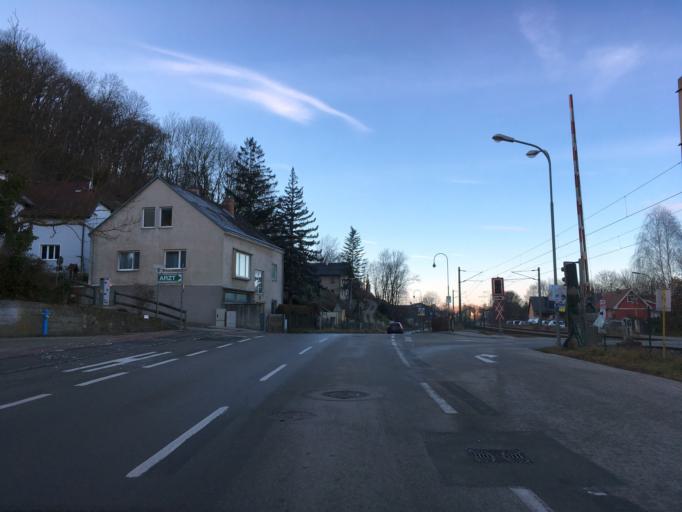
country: AT
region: Lower Austria
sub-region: Politischer Bezirk Korneuburg
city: Spillern
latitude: 48.3486
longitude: 16.2794
